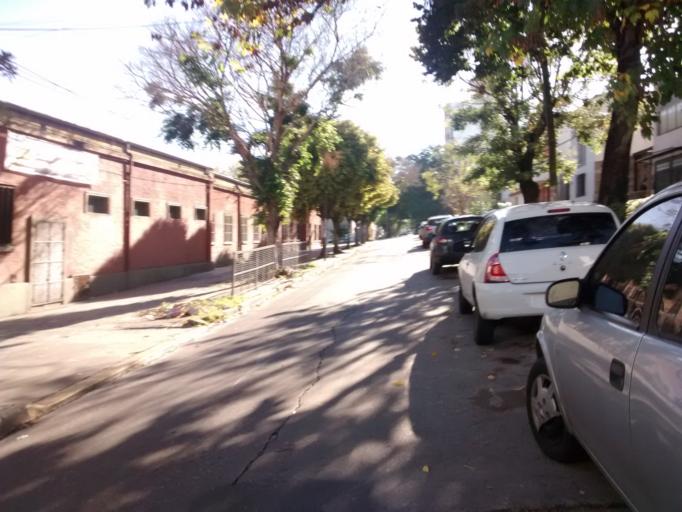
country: AR
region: Buenos Aires
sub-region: Partido de La Plata
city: La Plata
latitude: -34.9352
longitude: -57.9511
